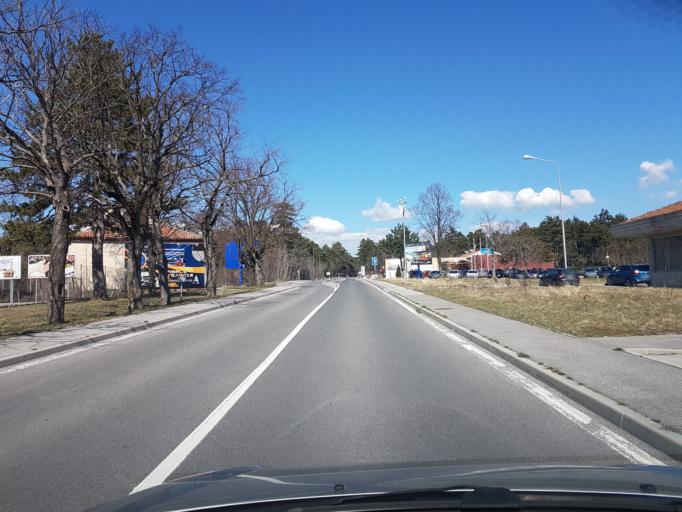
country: IT
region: Friuli Venezia Giulia
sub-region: Provincia di Trieste
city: Dolina
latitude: 45.6524
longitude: 13.8795
